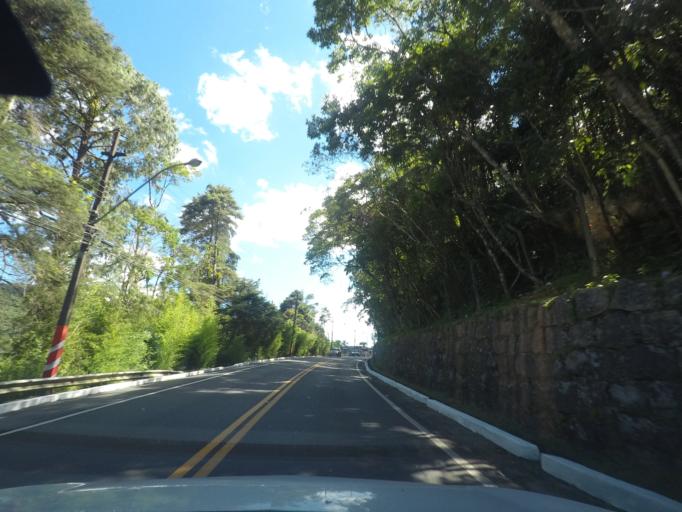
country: BR
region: Rio de Janeiro
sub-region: Teresopolis
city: Teresopolis
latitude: -22.4524
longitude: -42.9825
